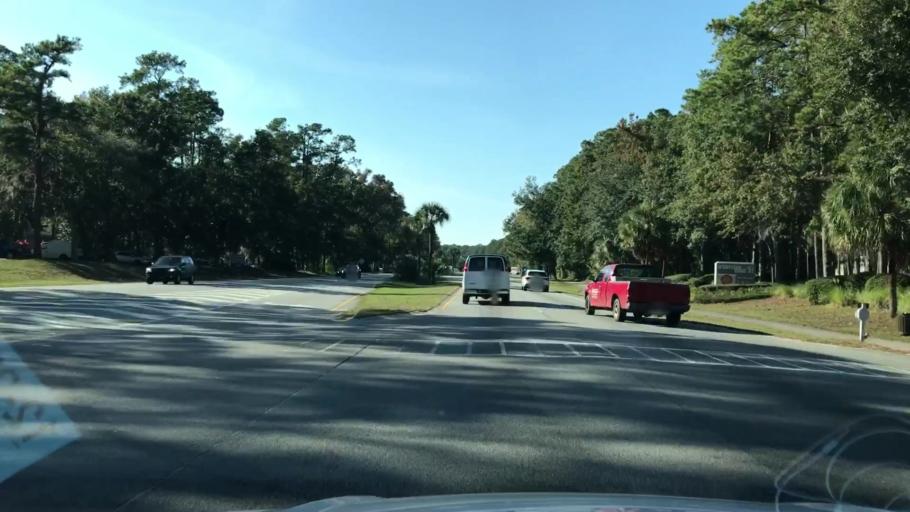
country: US
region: South Carolina
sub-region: Beaufort County
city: Hilton Head Island
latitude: 32.2164
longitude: -80.7085
